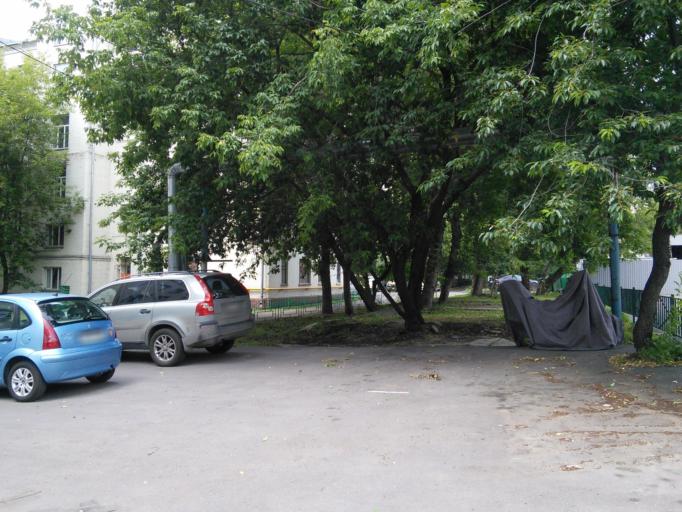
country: RU
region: Moscow
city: Luzhniki
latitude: 55.7253
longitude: 37.5698
